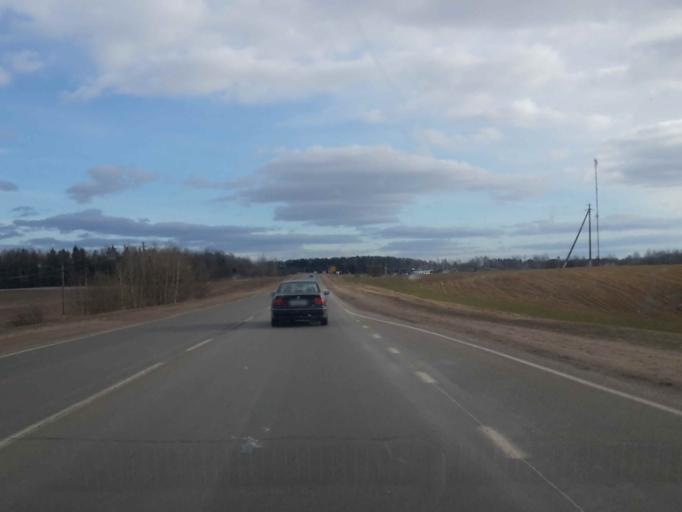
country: BY
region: Minsk
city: Bal'shavik
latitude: 54.0750
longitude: 27.5652
